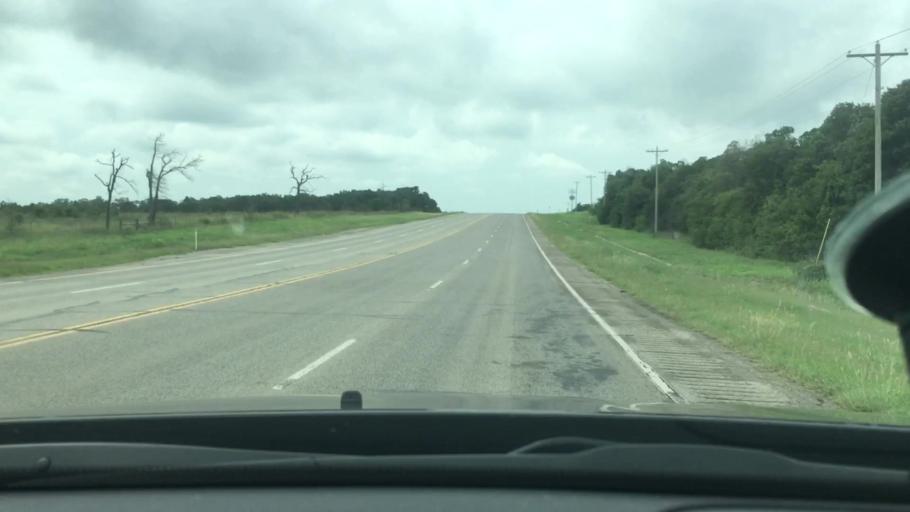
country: US
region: Oklahoma
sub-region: Carter County
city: Healdton
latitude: 34.1901
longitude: -97.4749
